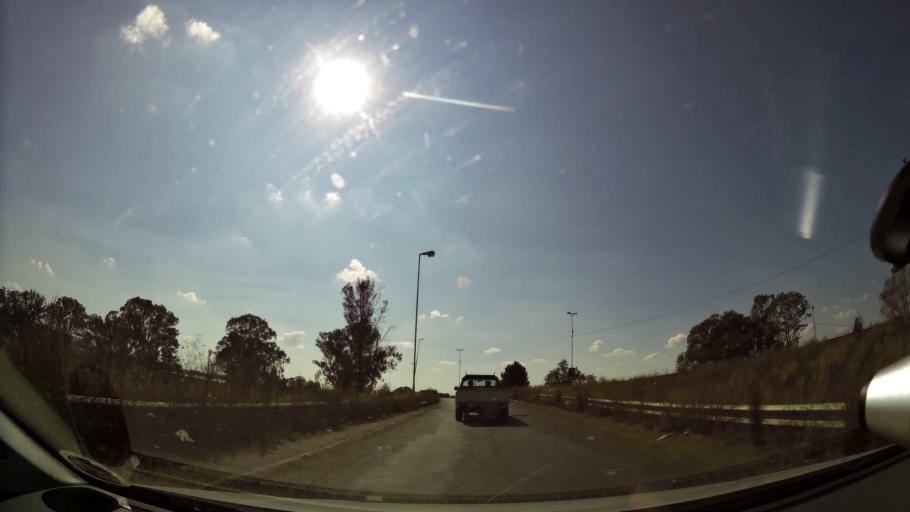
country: ZA
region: Orange Free State
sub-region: Mangaung Metropolitan Municipality
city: Bloemfontein
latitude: -29.1353
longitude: 26.2669
